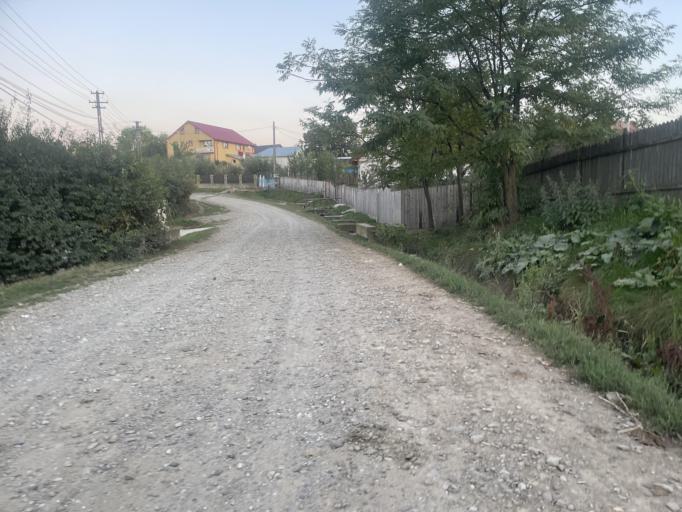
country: RO
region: Iasi
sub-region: Comuna Dumesti
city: Pausesti
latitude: 47.1545
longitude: 27.3211
